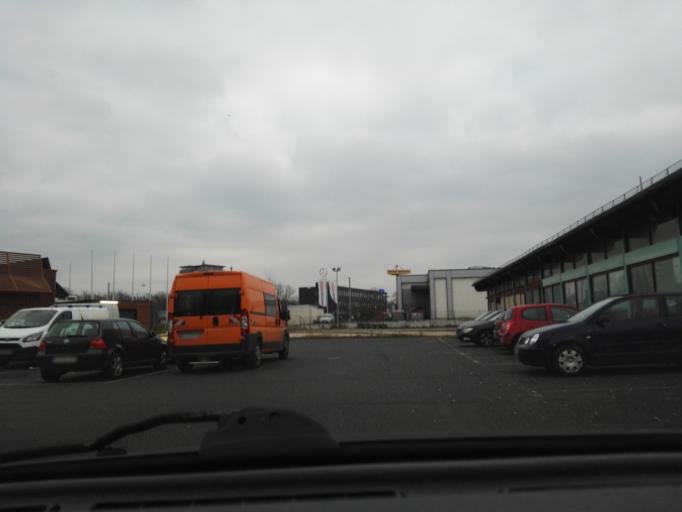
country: DE
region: Lower Saxony
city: Braunschweig
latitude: 52.2480
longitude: 10.5103
